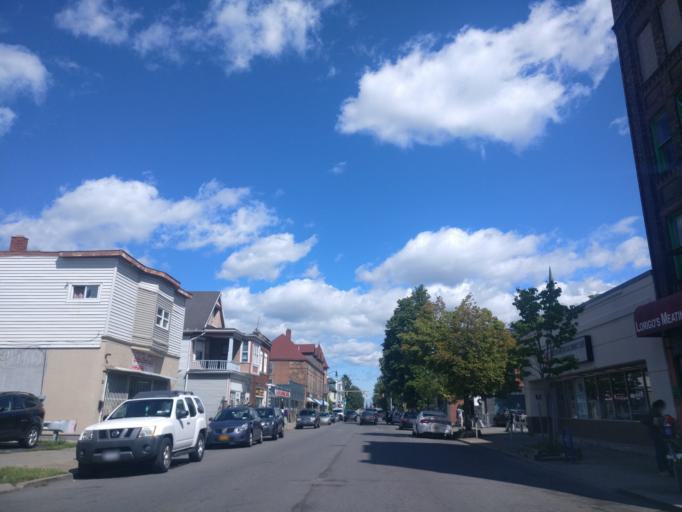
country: US
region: New York
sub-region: Erie County
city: Buffalo
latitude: 42.9189
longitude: -78.8906
